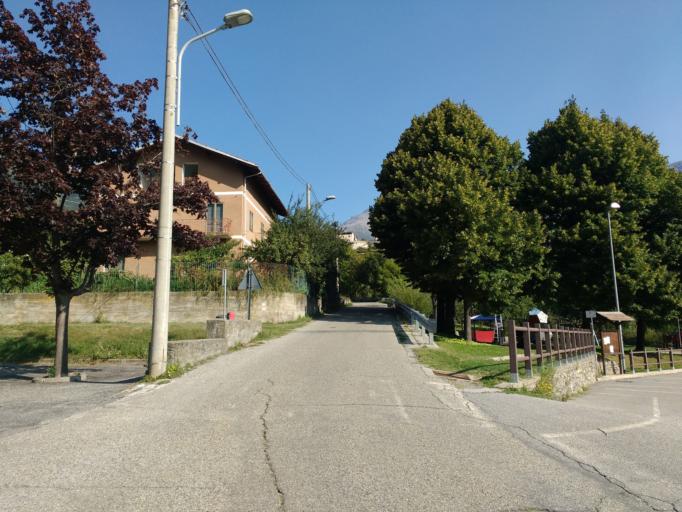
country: IT
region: Piedmont
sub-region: Provincia di Torino
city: Giaglione
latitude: 45.1385
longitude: 7.0160
